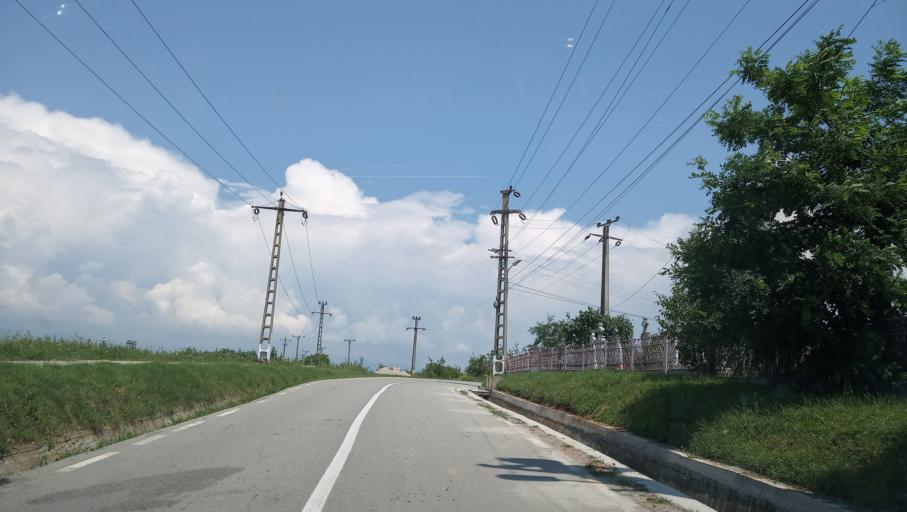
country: RO
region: Gorj
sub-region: Comuna Turcinesti
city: Turcinesti
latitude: 45.0456
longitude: 23.3433
